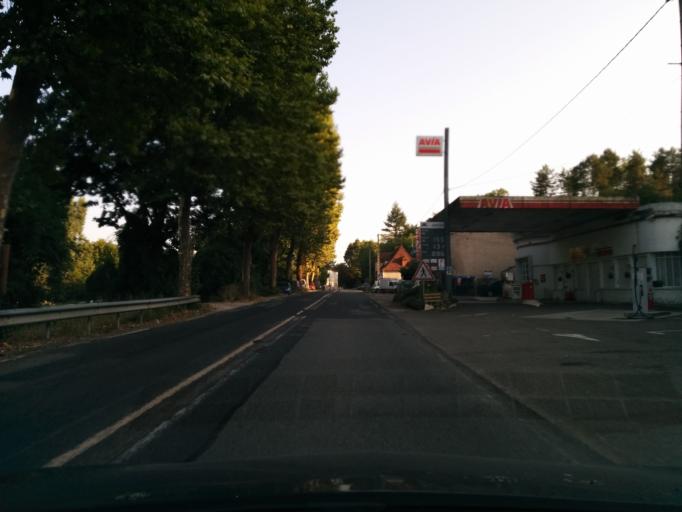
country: FR
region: Midi-Pyrenees
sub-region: Departement du Lot
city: Le Vigan
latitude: 44.6644
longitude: 1.4810
